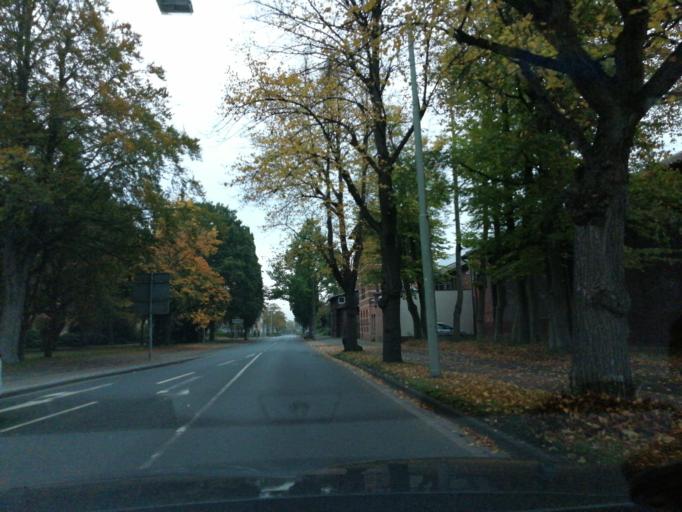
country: DE
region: Lower Saxony
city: Wilhelmshaven
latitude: 53.5181
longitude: 8.1235
